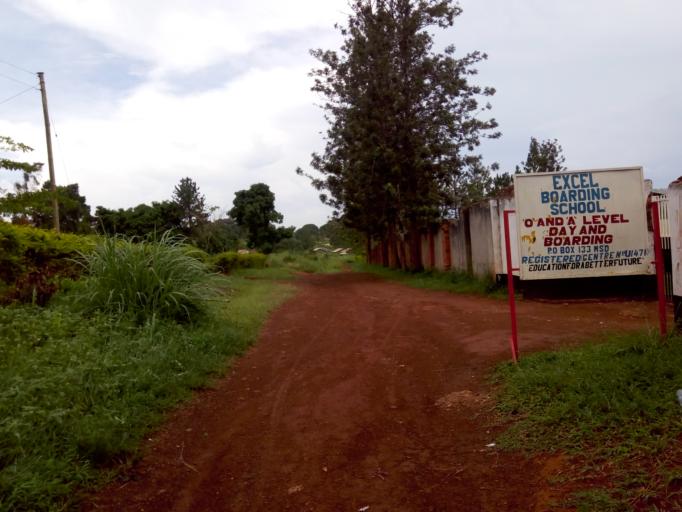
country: UG
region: Western Region
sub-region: Masindi District
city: Masindi
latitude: 1.6890
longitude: 31.7127
